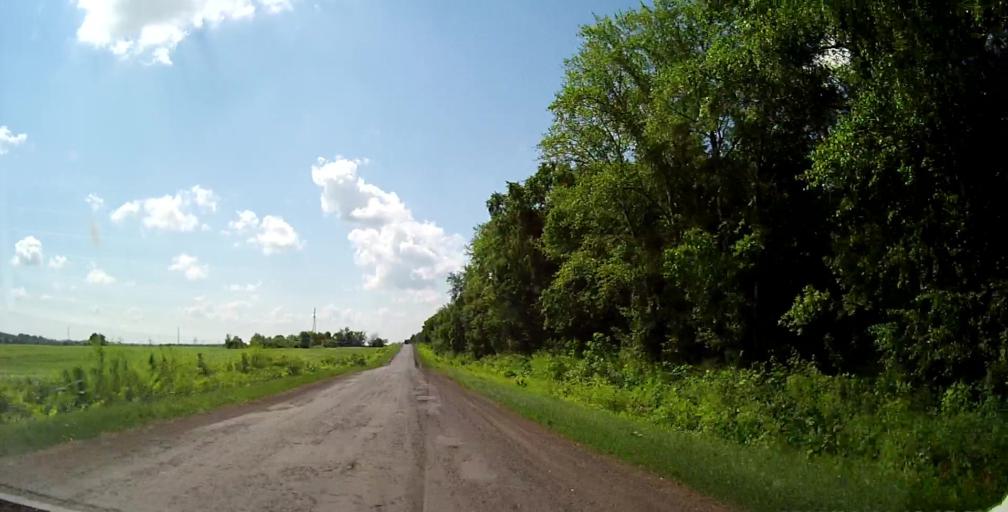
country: RU
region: Lipetsk
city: Chaplygin
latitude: 53.2961
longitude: 39.9554
